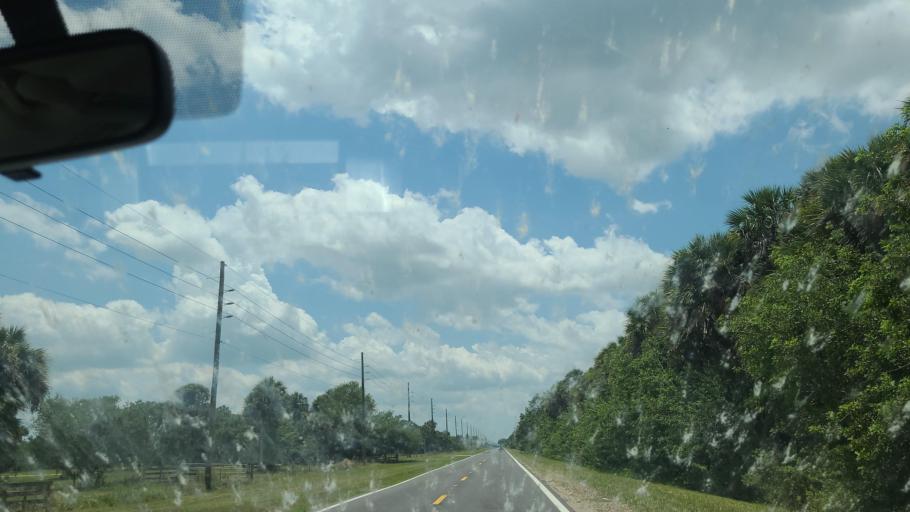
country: US
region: Florida
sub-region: Glades County
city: Buckhead Ridge
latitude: 27.2207
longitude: -81.0952
